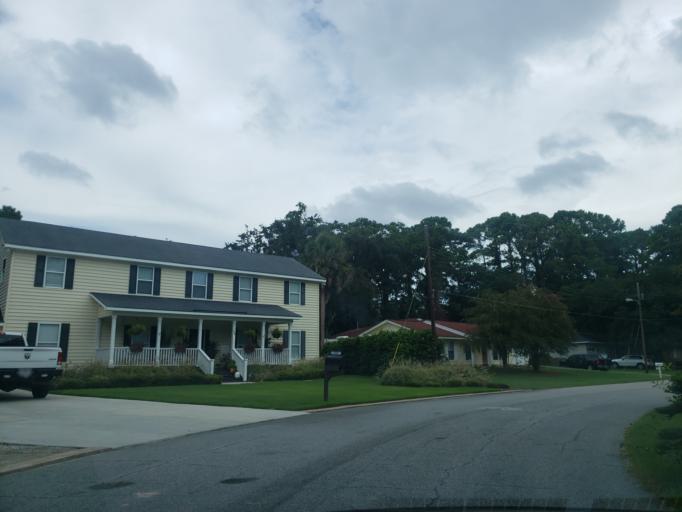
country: US
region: Georgia
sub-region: Chatham County
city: Wilmington Island
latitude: 32.0052
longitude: -80.9630
